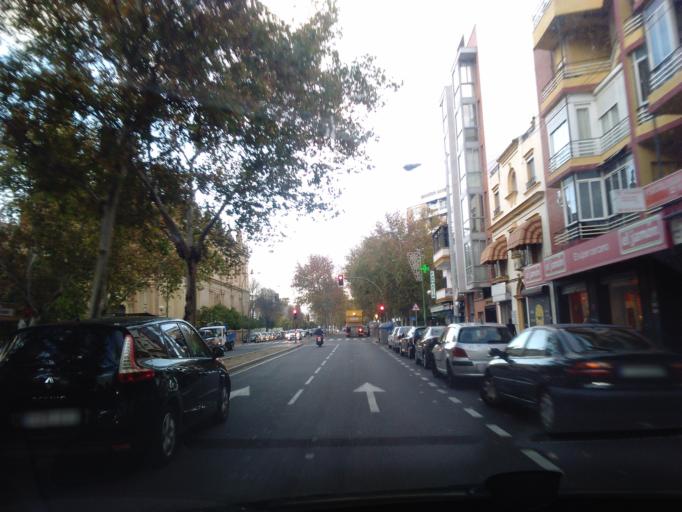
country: ES
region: Andalusia
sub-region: Provincia de Sevilla
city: Sevilla
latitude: 37.3825
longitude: -5.9656
